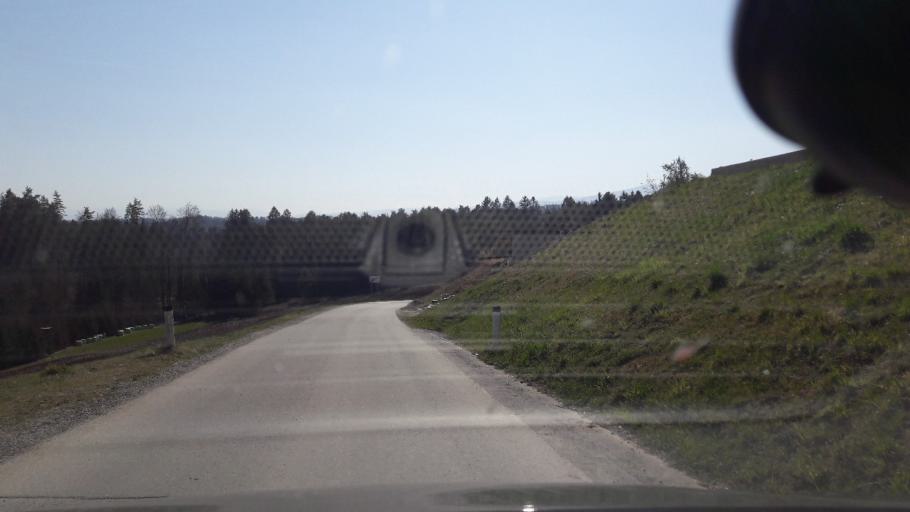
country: AT
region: Styria
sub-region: Politischer Bezirk Graz-Umgebung
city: Hitzendorf
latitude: 47.0337
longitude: 15.3145
